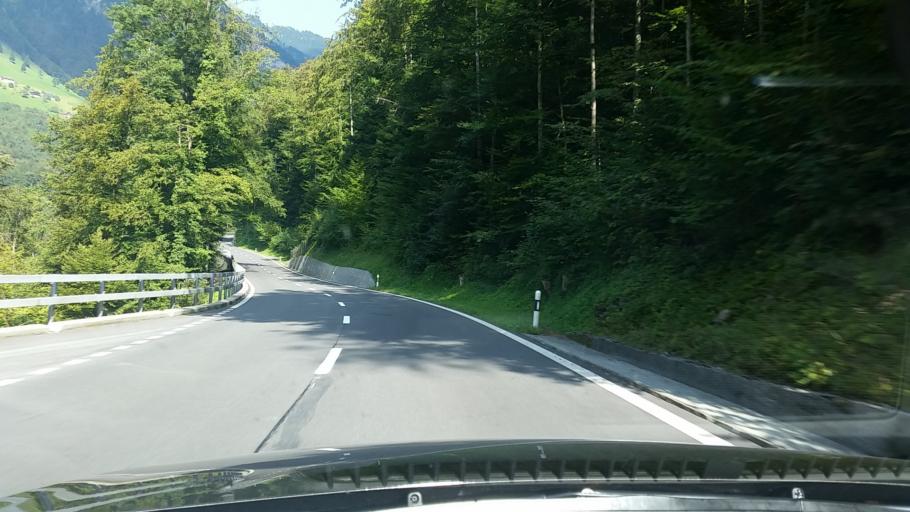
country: CH
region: Obwalden
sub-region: Obwalden
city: Engelberg
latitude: 46.8520
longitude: 8.3731
